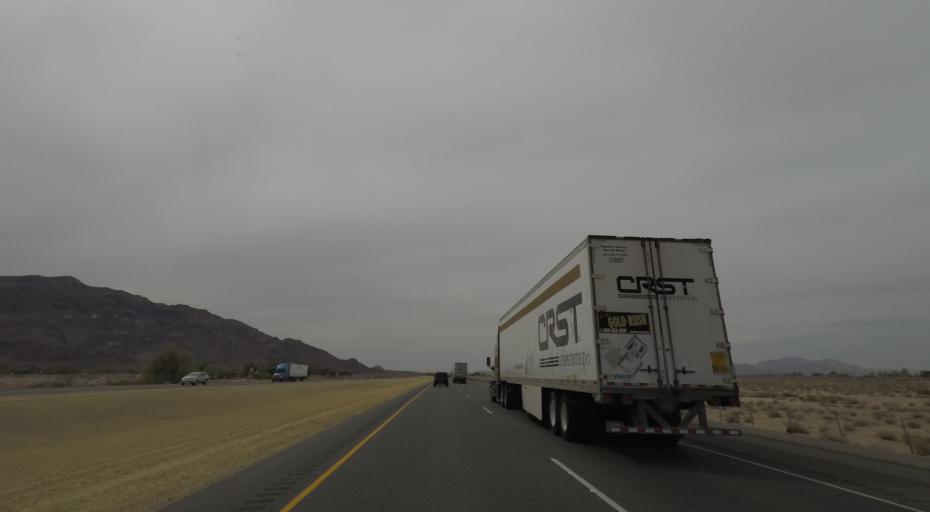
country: US
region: California
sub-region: San Bernardino County
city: Barstow
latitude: 34.8232
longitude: -116.6472
